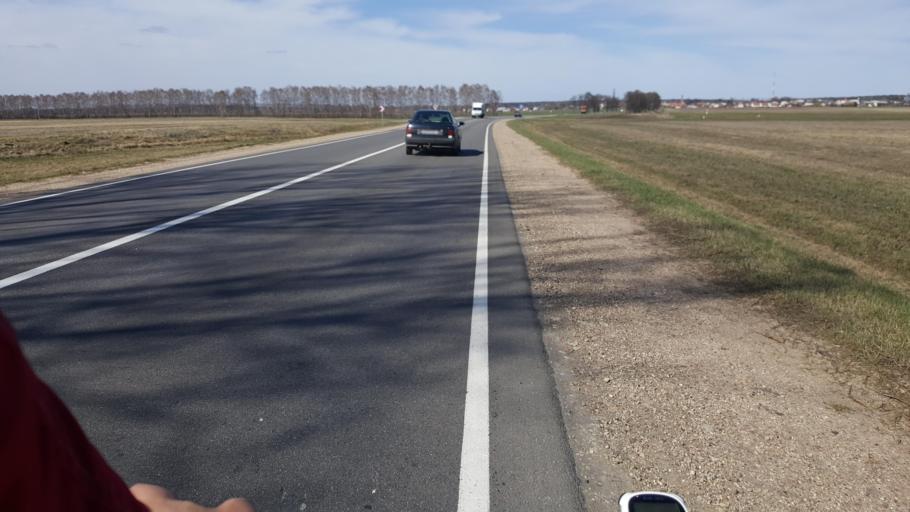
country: BY
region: Brest
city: Kamyanyets
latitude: 52.3100
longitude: 23.7809
